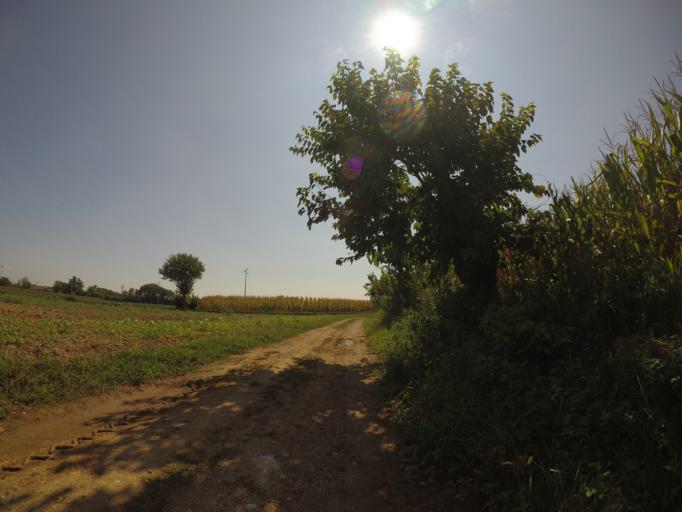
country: IT
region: Friuli Venezia Giulia
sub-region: Provincia di Udine
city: Talmassons
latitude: 45.9409
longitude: 13.0933
